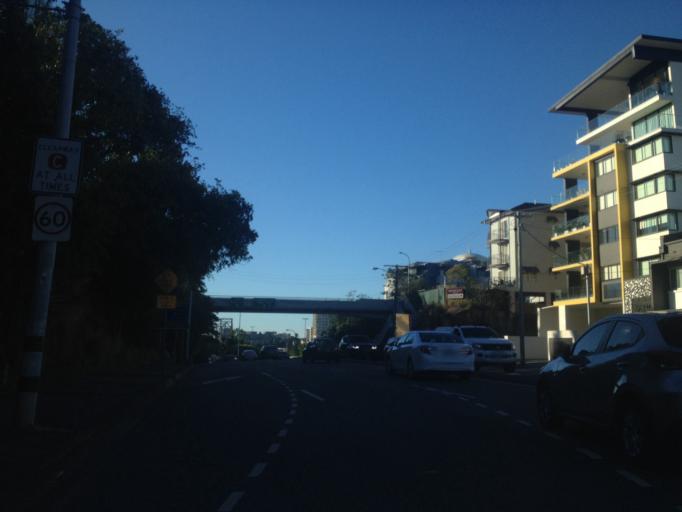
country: AU
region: Queensland
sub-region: Brisbane
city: Brisbane
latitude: -27.4760
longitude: 153.0355
